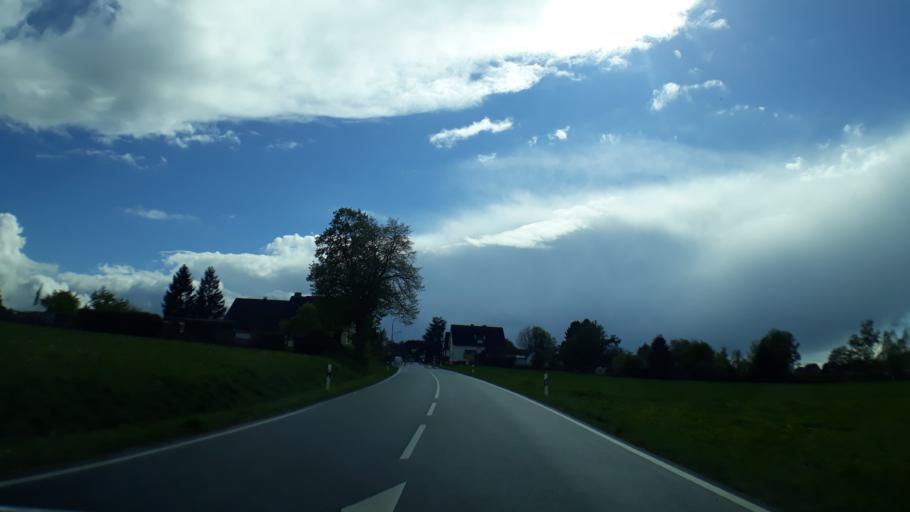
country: DE
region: North Rhine-Westphalia
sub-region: Regierungsbezirk Koln
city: Schleiden
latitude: 50.4979
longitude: 6.5245
